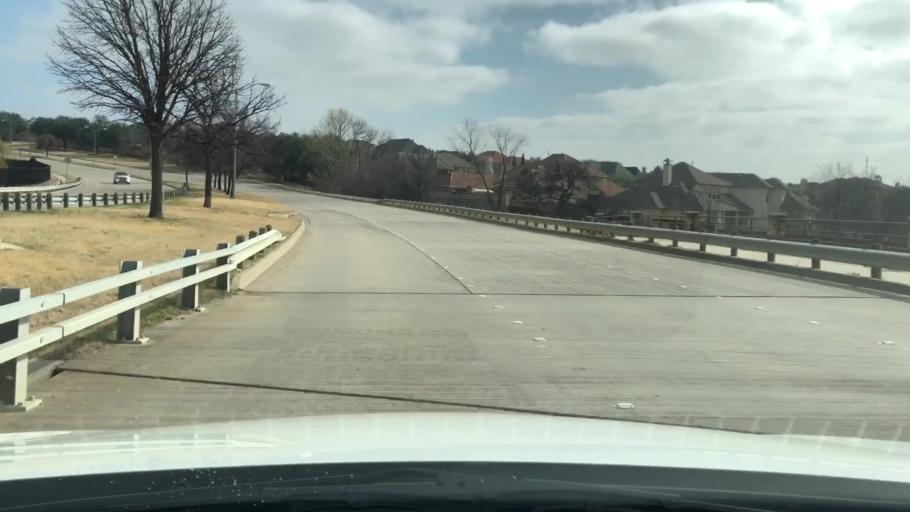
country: US
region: Texas
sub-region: Denton County
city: The Colony
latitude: 33.0700
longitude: -96.8496
